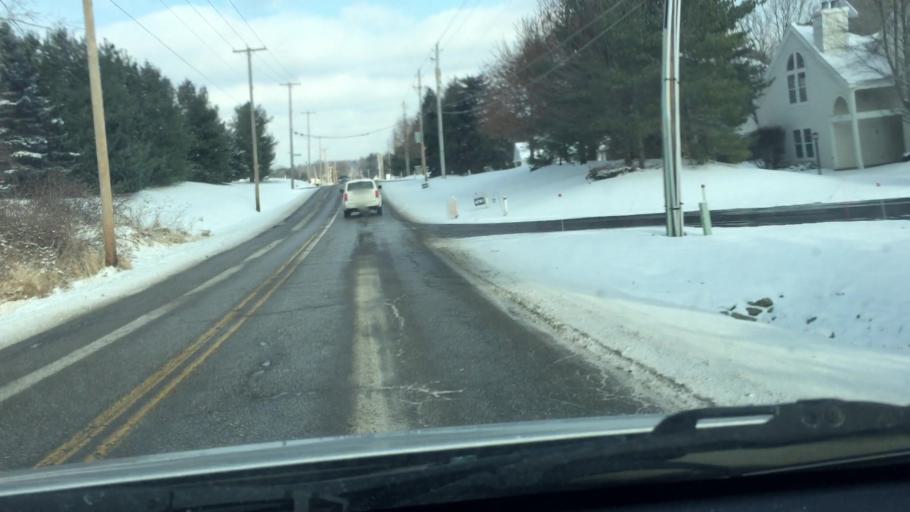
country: US
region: Ohio
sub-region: Mahoning County
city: Boardman
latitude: 41.0201
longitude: -80.7113
